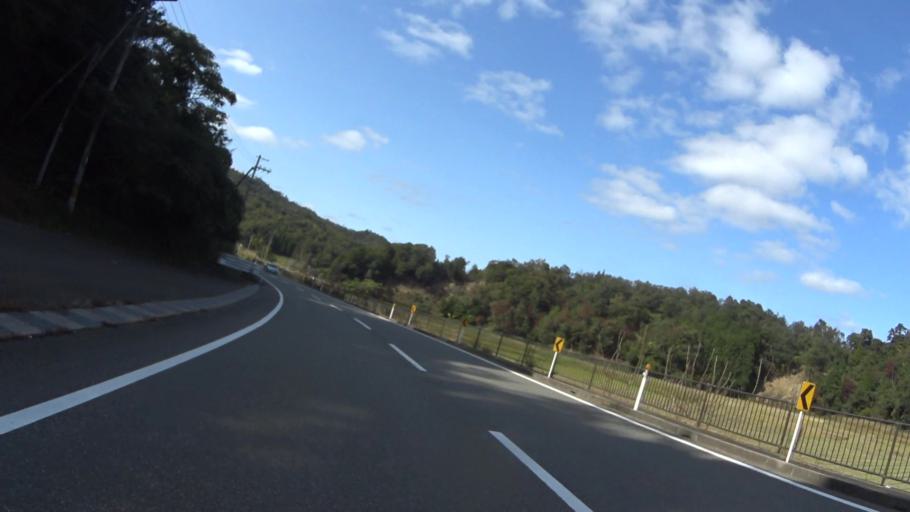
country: JP
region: Hyogo
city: Toyooka
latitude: 35.5643
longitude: 134.9779
